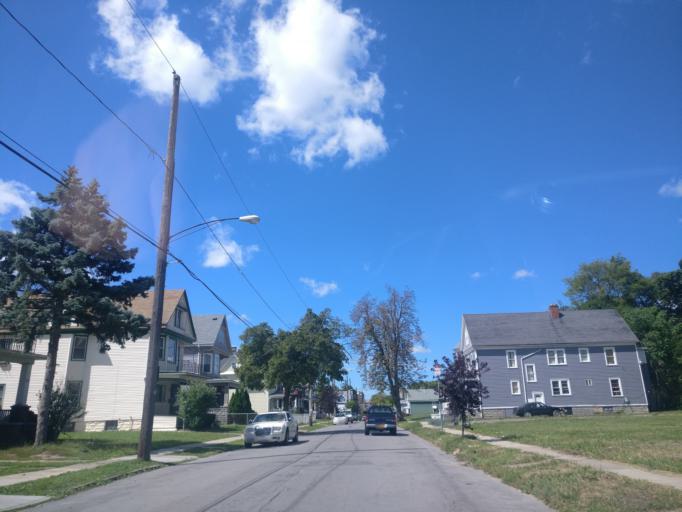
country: US
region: New York
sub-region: Erie County
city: Buffalo
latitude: 42.9094
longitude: -78.8570
